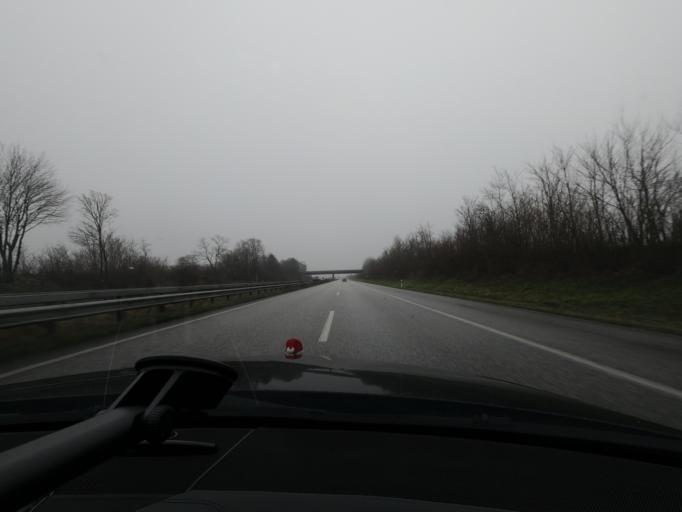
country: DE
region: Schleswig-Holstein
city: Bollingstedt
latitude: 54.6400
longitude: 9.4381
